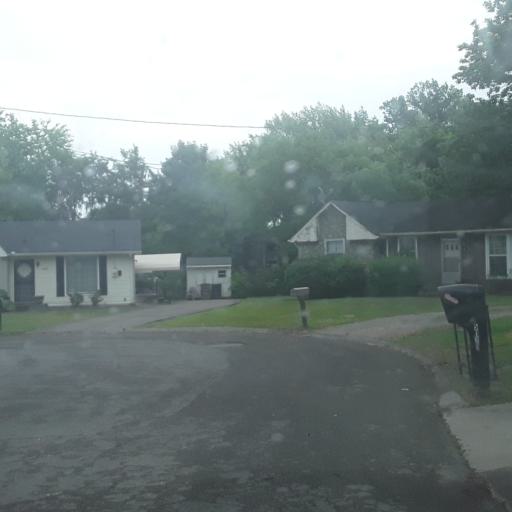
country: US
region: Tennessee
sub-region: Williamson County
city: Brentwood
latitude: 36.0563
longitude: -86.7212
